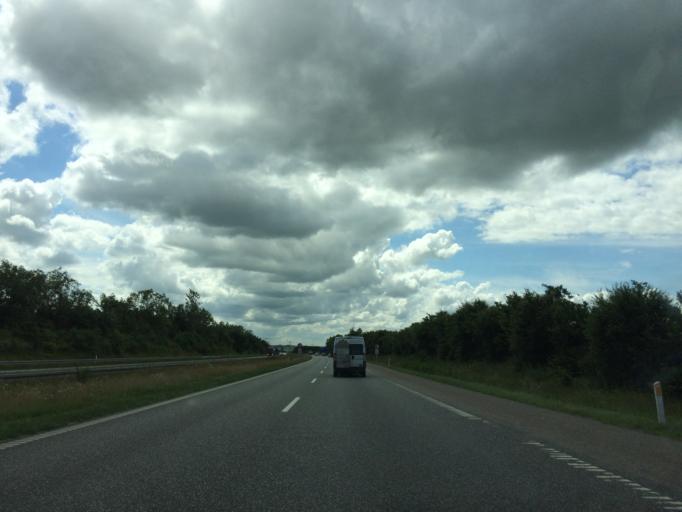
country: DK
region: North Denmark
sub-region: Rebild Kommune
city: Stovring
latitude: 56.8385
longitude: 9.7360
